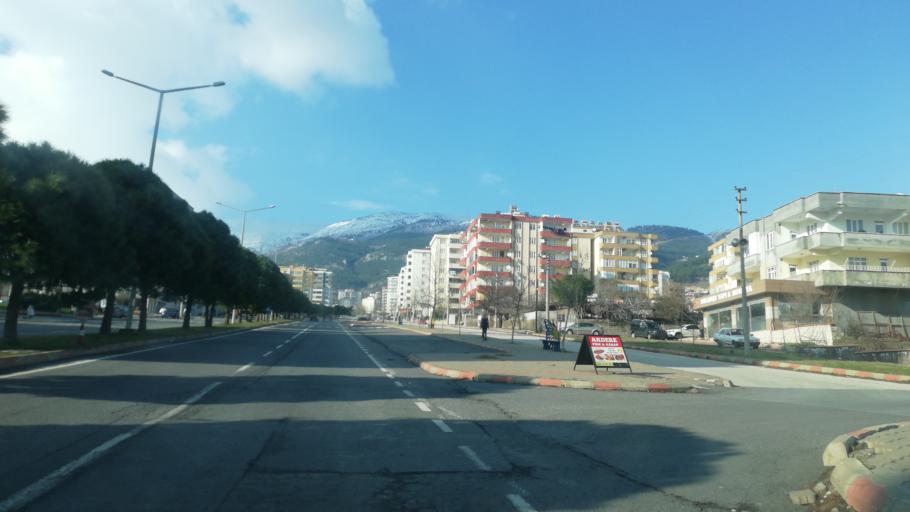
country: TR
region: Kahramanmaras
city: Kahramanmaras
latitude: 37.5938
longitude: 36.8987
